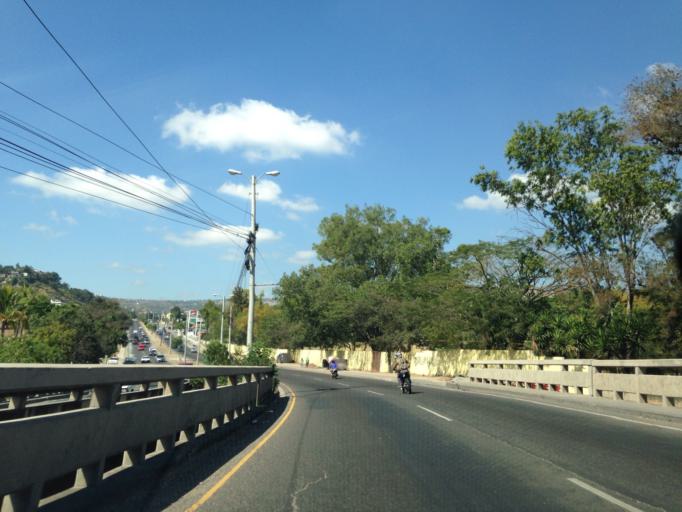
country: HN
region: Francisco Morazan
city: Tegucigalpa
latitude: 14.0854
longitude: -87.2191
